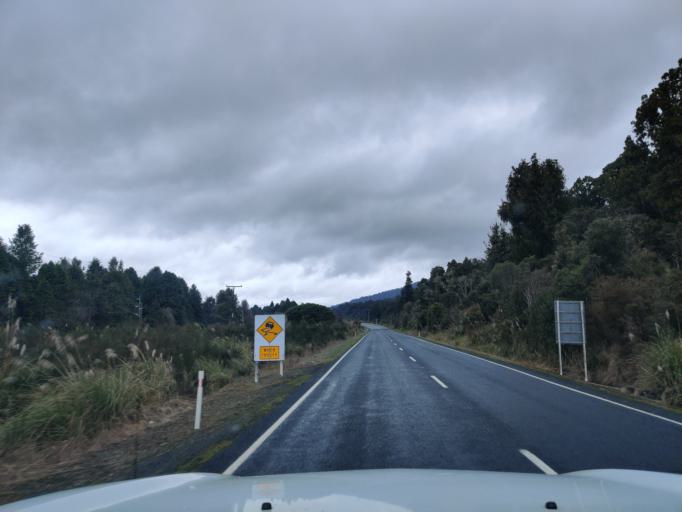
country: NZ
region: Manawatu-Wanganui
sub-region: Ruapehu District
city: Waiouru
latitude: -39.2454
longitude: 175.3899
